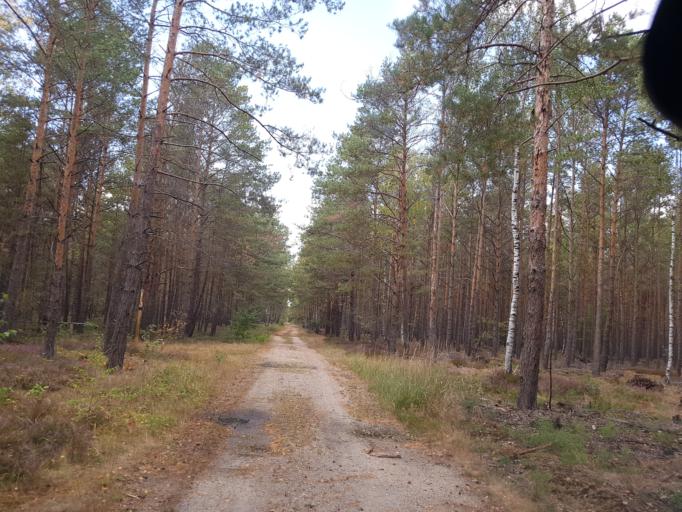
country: DE
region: Brandenburg
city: Finsterwalde
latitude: 51.5899
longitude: 13.7513
